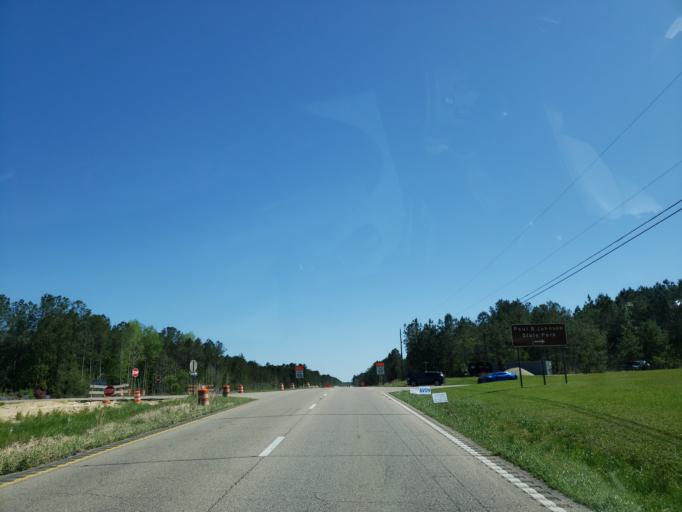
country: US
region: Mississippi
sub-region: Lamar County
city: Purvis
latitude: 31.1356
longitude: -89.2301
